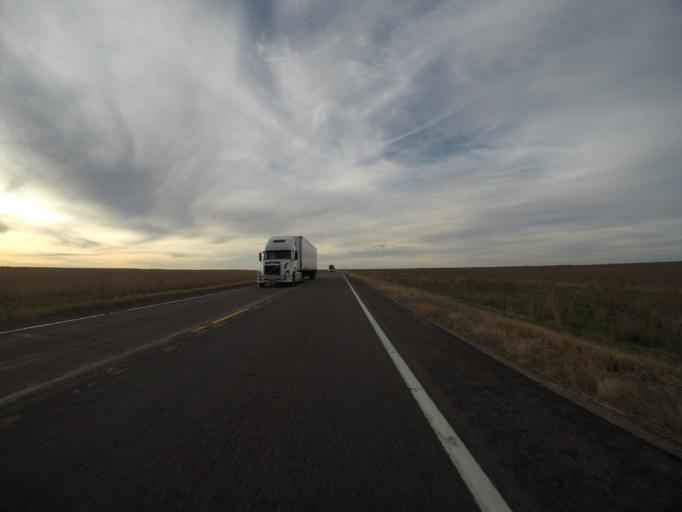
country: US
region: Colorado
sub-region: Yuma County
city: Yuma
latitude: 39.6939
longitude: -102.9842
